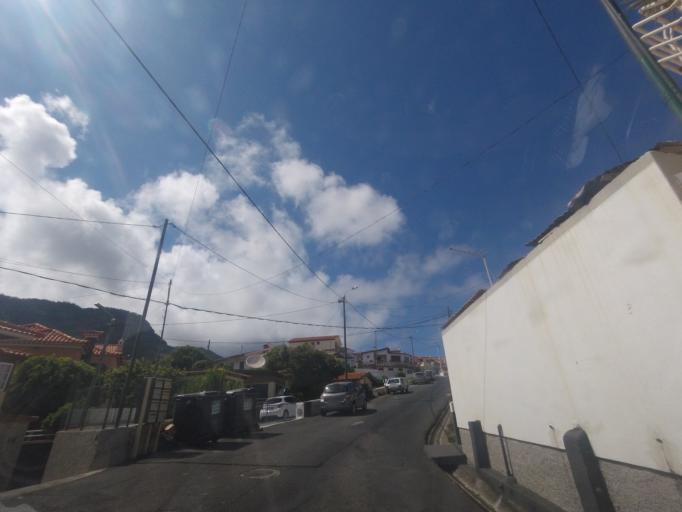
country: PT
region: Madeira
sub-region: Machico
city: Canical
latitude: 32.7384
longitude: -16.7380
